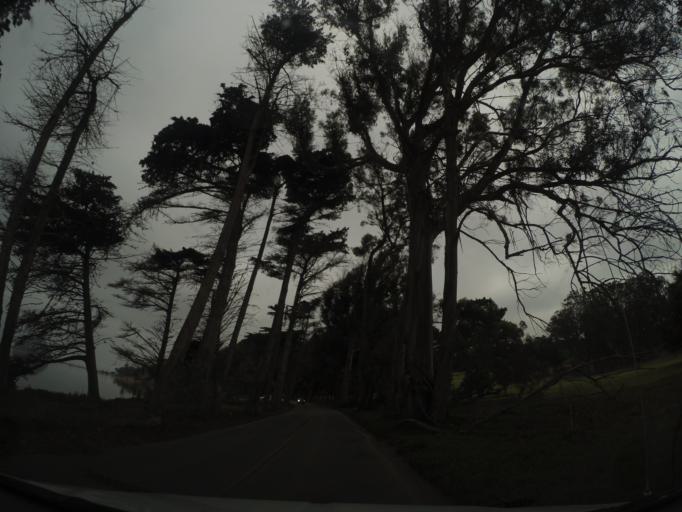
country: US
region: California
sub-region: San Luis Obispo County
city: Morro Bay
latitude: 35.3484
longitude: -120.8434
